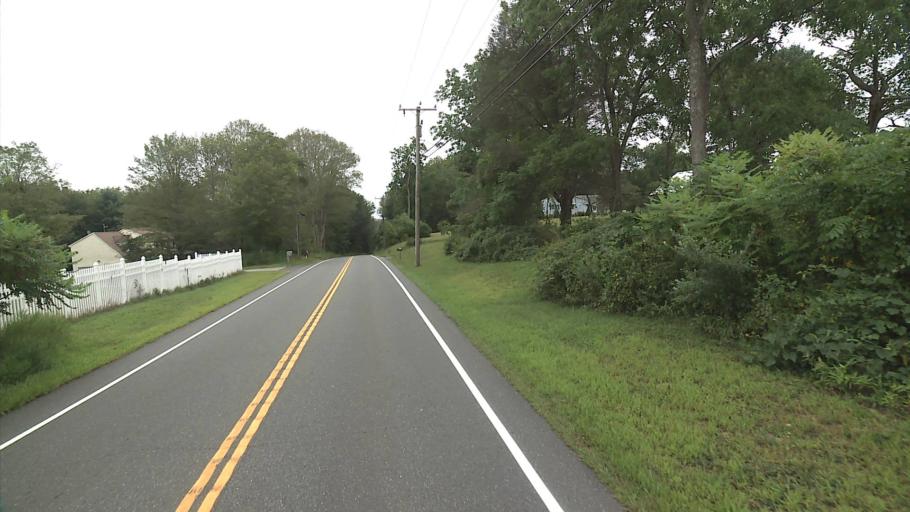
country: US
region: Connecticut
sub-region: New London County
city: Colchester
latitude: 41.5134
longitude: -72.2921
